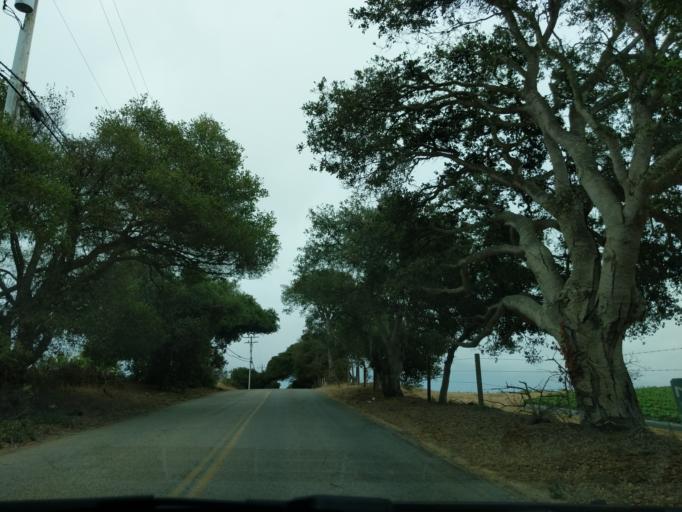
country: US
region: California
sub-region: Monterey County
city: Prunedale
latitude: 36.7887
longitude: -121.6918
